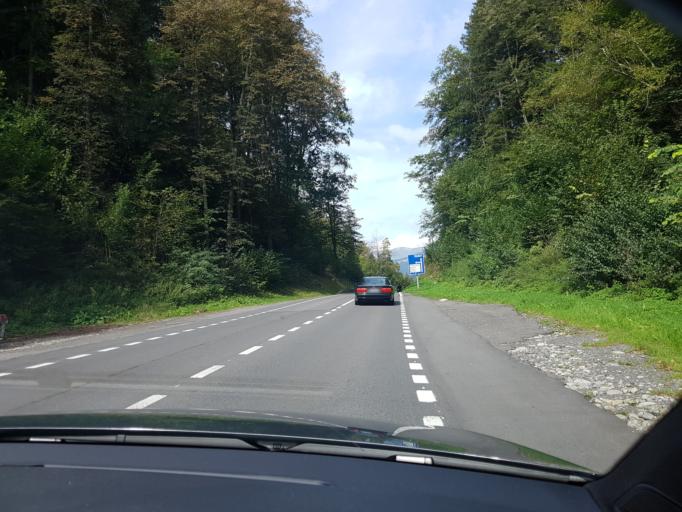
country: CH
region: Bern
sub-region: Interlaken-Oberhasli District
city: Meiringen
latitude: 46.7128
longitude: 8.2130
